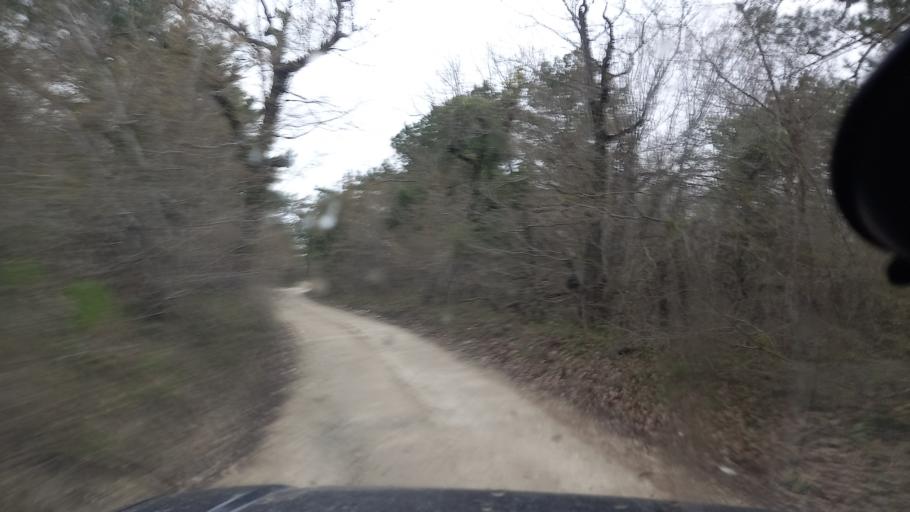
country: RU
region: Krasnodarskiy
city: Dzhubga
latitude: 44.3197
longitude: 38.6877
